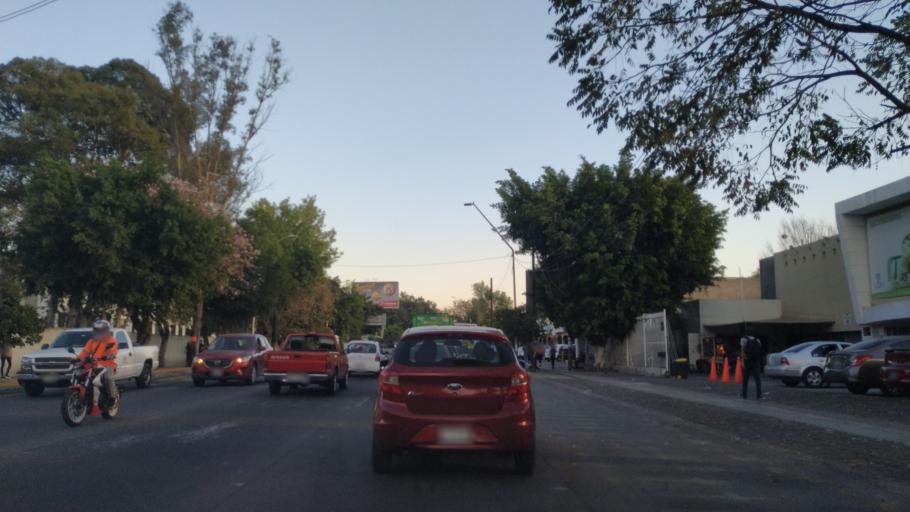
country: MX
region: Jalisco
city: Tlaquepaque
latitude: 20.6544
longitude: -103.3267
